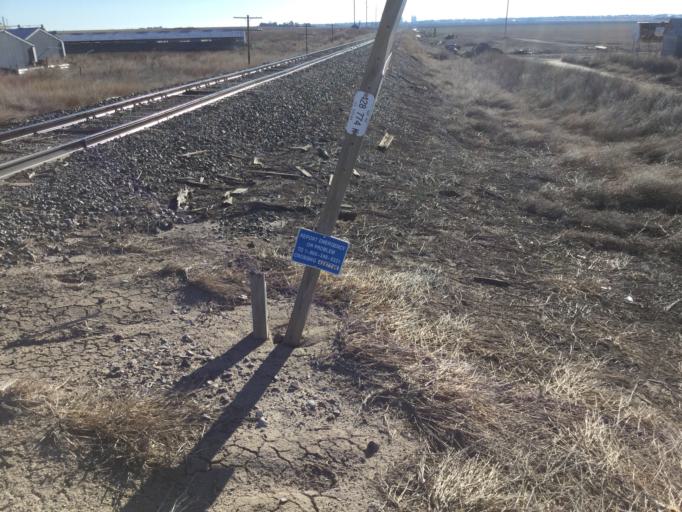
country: US
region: Kansas
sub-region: Scott County
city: Scott City
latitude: 38.4870
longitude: -100.9624
